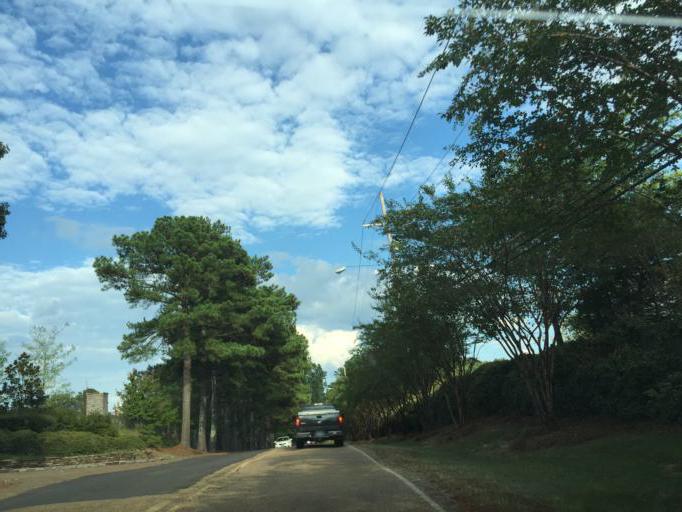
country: US
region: Mississippi
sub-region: Madison County
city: Madison
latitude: 32.4651
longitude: -90.0740
